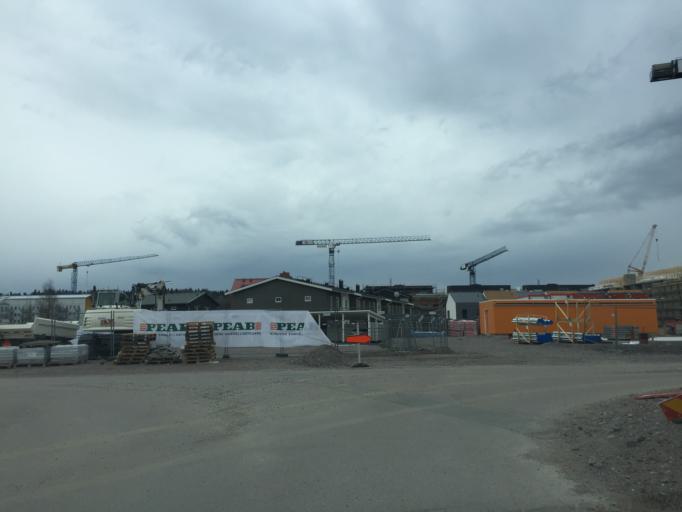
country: SE
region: OErebro
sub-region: Orebro Kommun
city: Orebro
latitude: 59.2547
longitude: 15.2186
